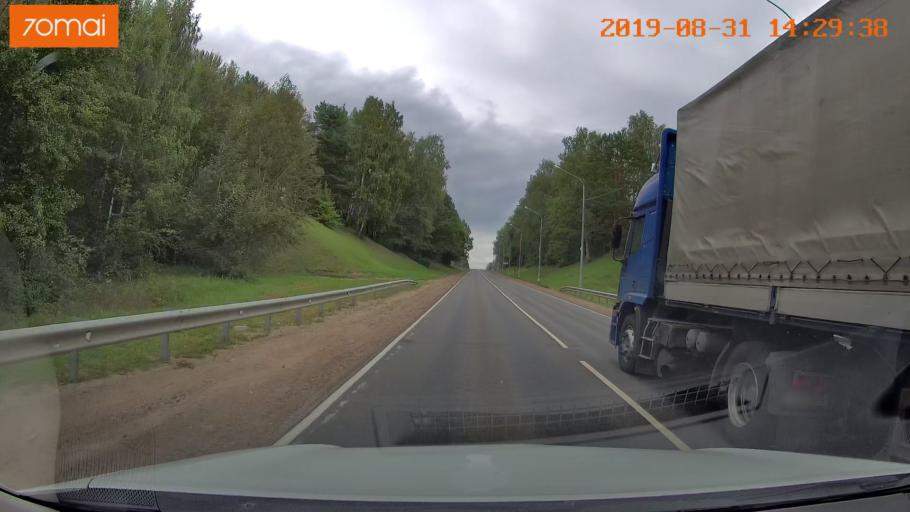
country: RU
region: Smolensk
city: Yekimovichi
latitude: 54.1270
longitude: 33.3356
